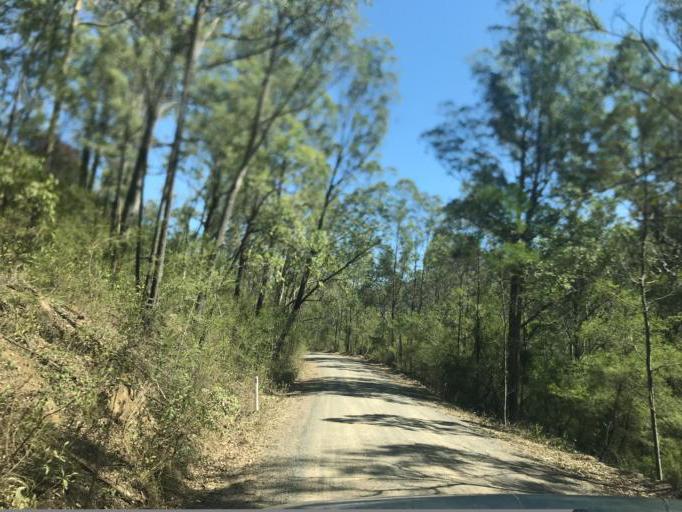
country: AU
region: New South Wales
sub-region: Wyong Shire
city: Little Jilliby
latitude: -33.1632
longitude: 151.0690
